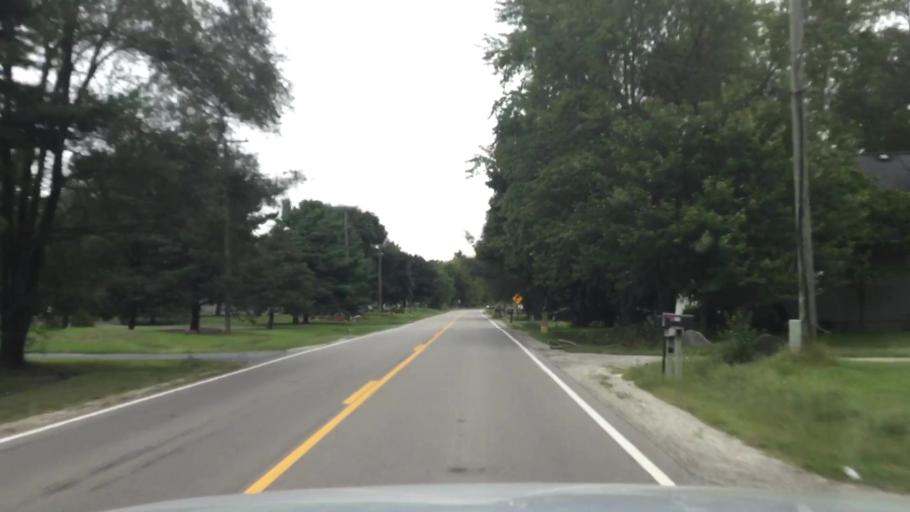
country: US
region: Michigan
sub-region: Washtenaw County
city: Ypsilanti
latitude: 42.1925
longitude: -83.6328
